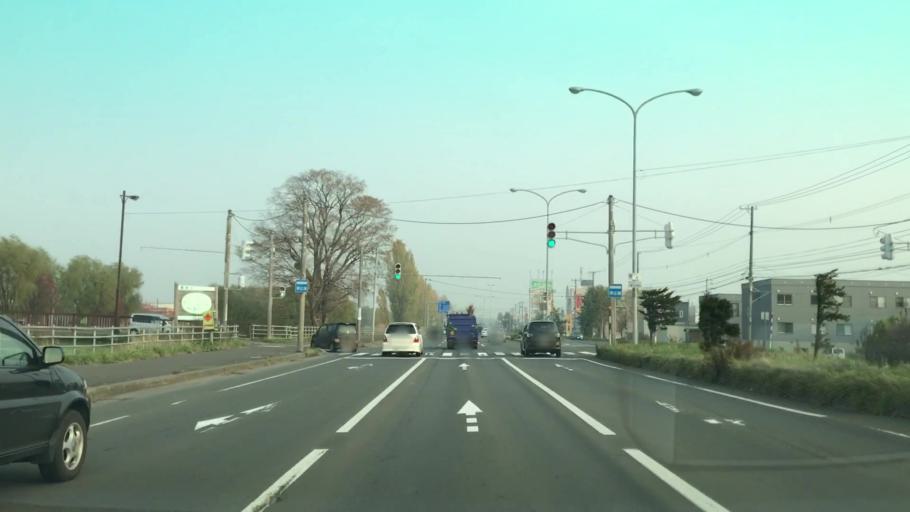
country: JP
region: Hokkaido
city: Ishikari
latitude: 43.1545
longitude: 141.3519
